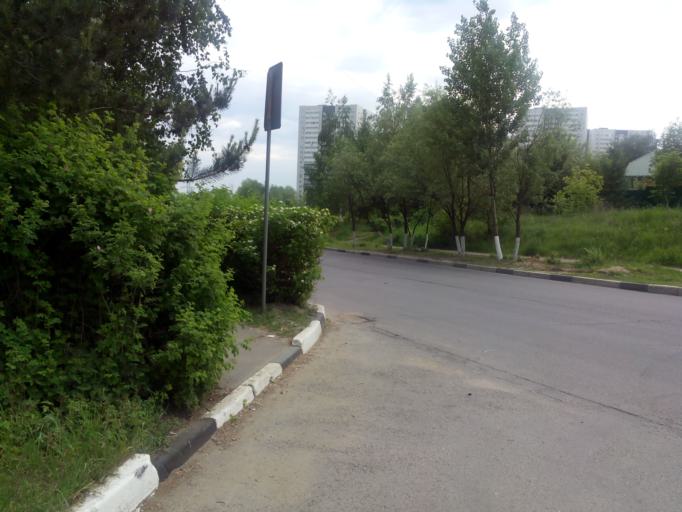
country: RU
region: Moskovskaya
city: Odintsovo
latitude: 55.6631
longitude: 37.2927
